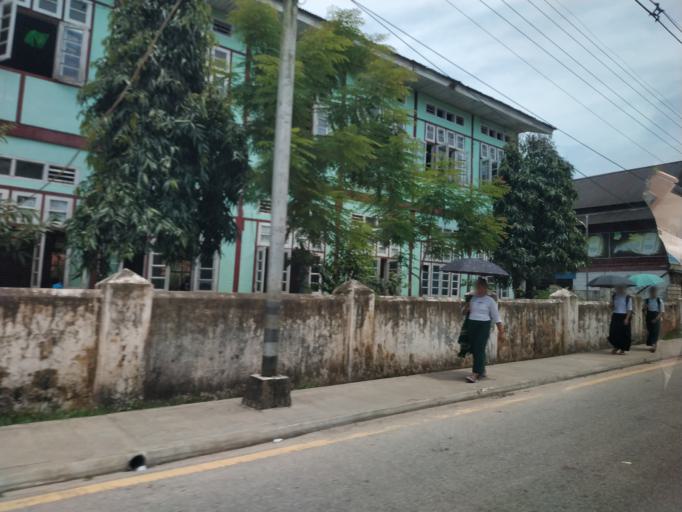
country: MM
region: Tanintharyi
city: Dawei
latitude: 14.0733
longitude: 98.1974
